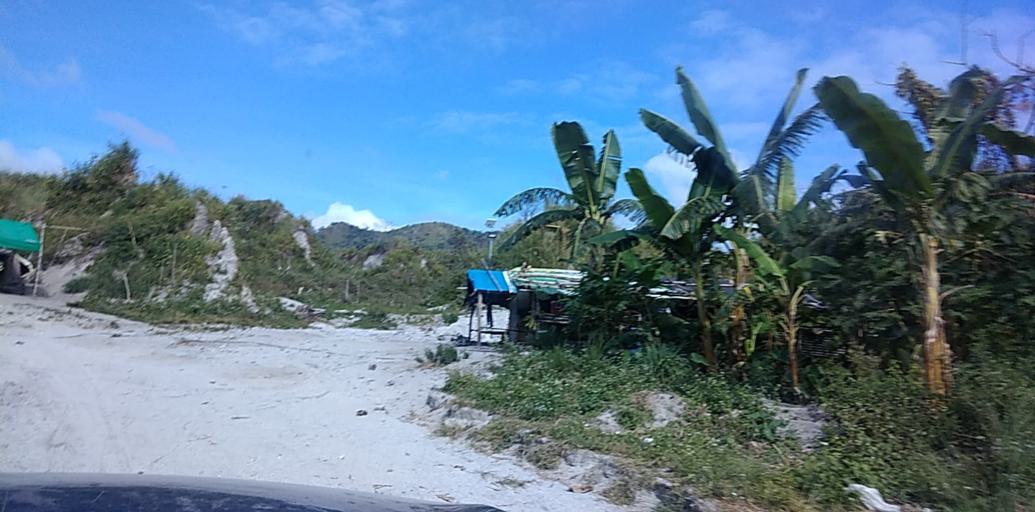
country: PH
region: Central Luzon
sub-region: Province of Pampanga
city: Babo-Pangulo
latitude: 15.1500
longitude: 120.4365
